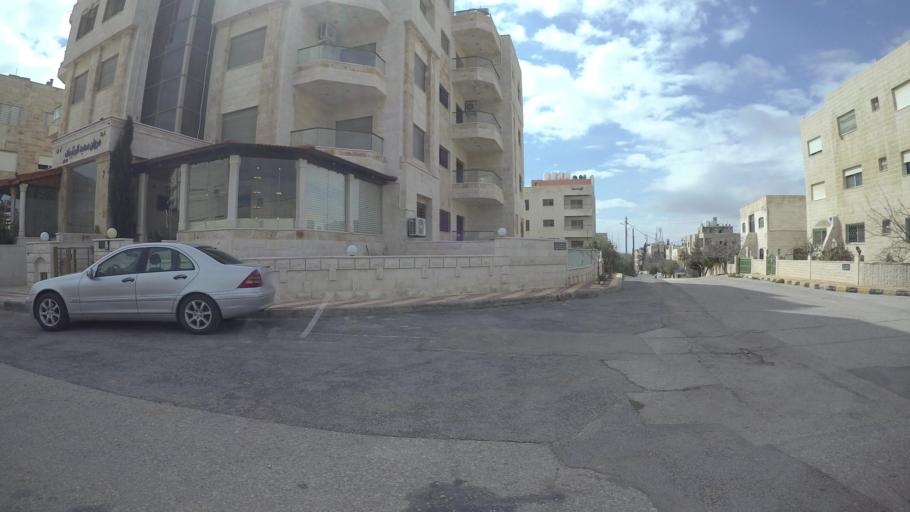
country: JO
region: Amman
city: Al Jubayhah
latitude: 32.0037
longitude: 35.8348
